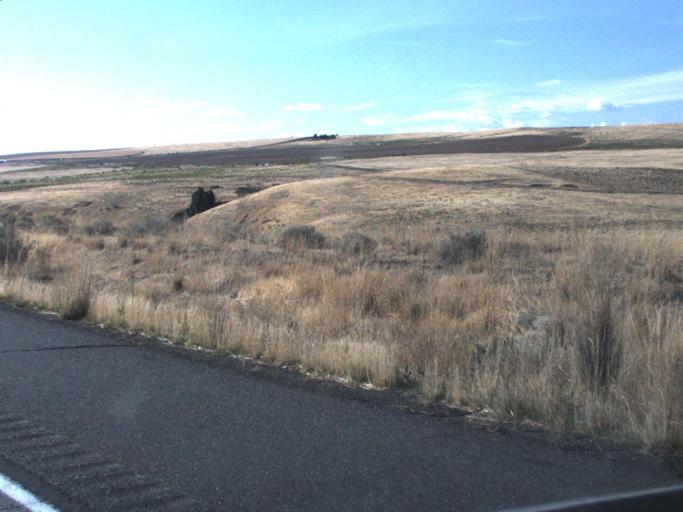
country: US
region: Oregon
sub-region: Umatilla County
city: Umatilla
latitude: 45.9840
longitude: -119.3140
